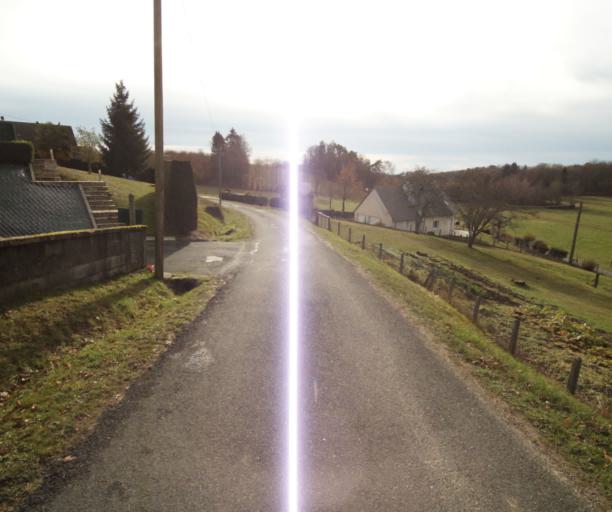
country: FR
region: Limousin
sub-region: Departement de la Correze
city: Saint-Mexant
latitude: 45.2677
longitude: 1.6798
